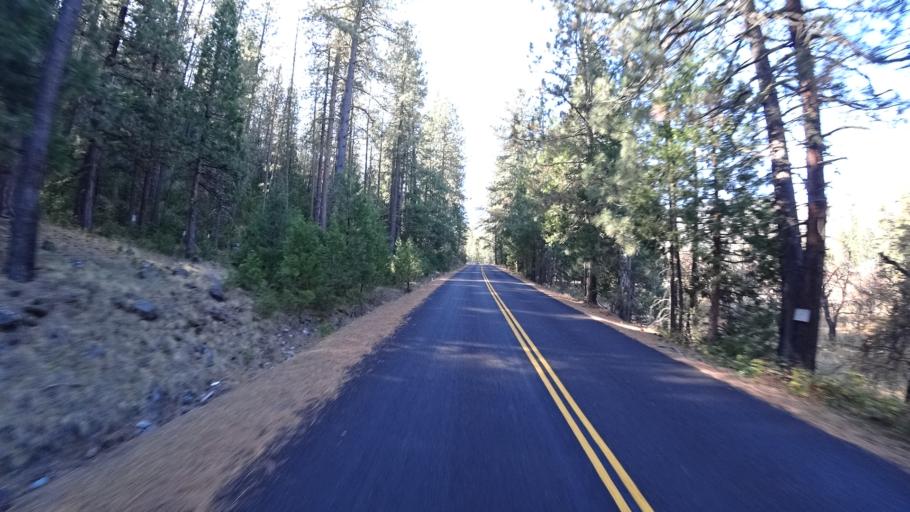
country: US
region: California
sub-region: Siskiyou County
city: Weed
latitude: 41.4334
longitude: -122.4798
